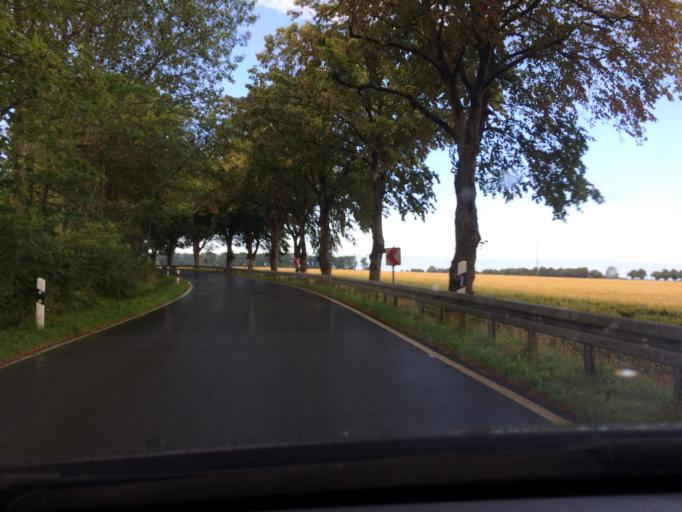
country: DE
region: Mecklenburg-Vorpommern
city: Altenpleen
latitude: 54.3973
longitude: 12.9696
